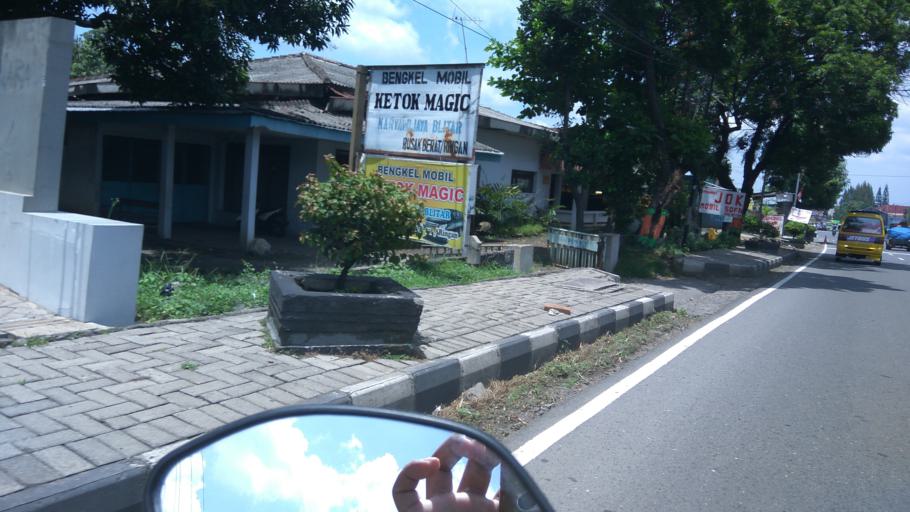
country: ID
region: Central Java
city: Ungaran
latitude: -7.1503
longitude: 110.4088
